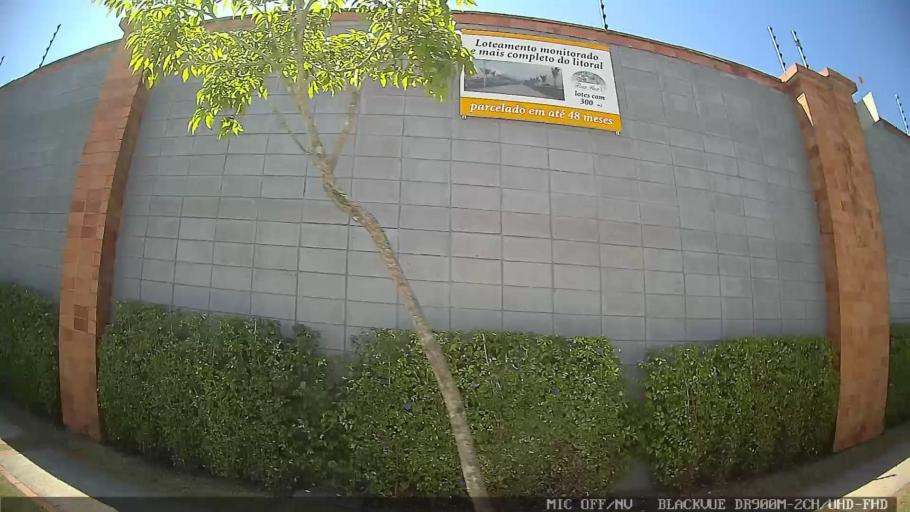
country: BR
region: Sao Paulo
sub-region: Peruibe
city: Peruibe
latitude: -24.3044
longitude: -46.9948
